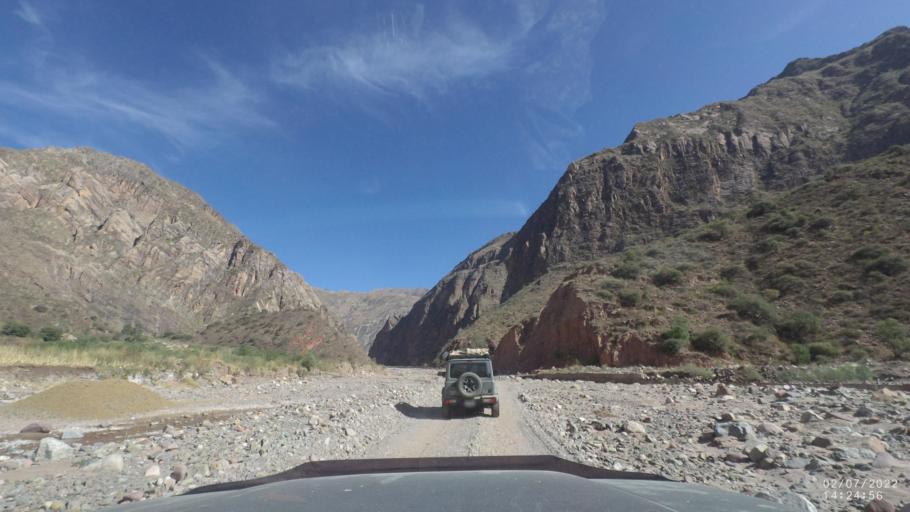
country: BO
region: Cochabamba
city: Irpa Irpa
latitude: -17.8339
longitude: -66.4141
